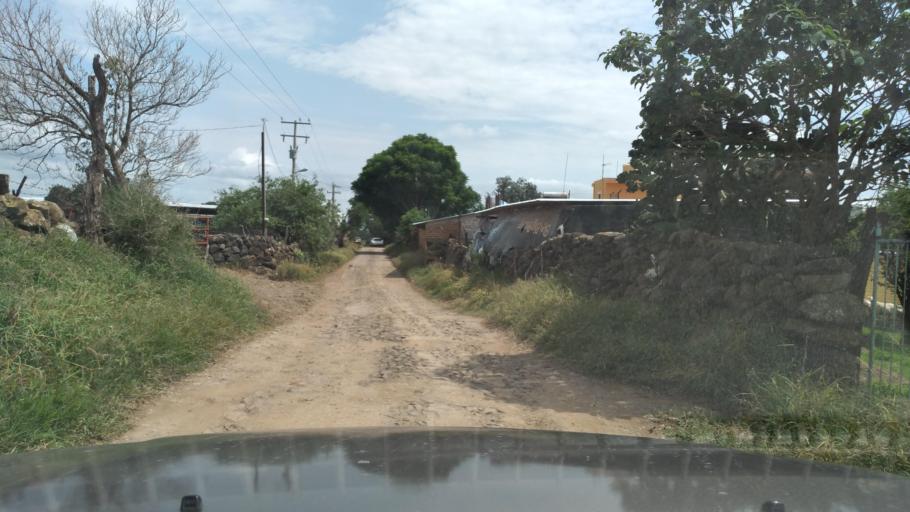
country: MX
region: Jalisco
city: Capilla de Guadalupe
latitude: 20.7484
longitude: -102.6325
